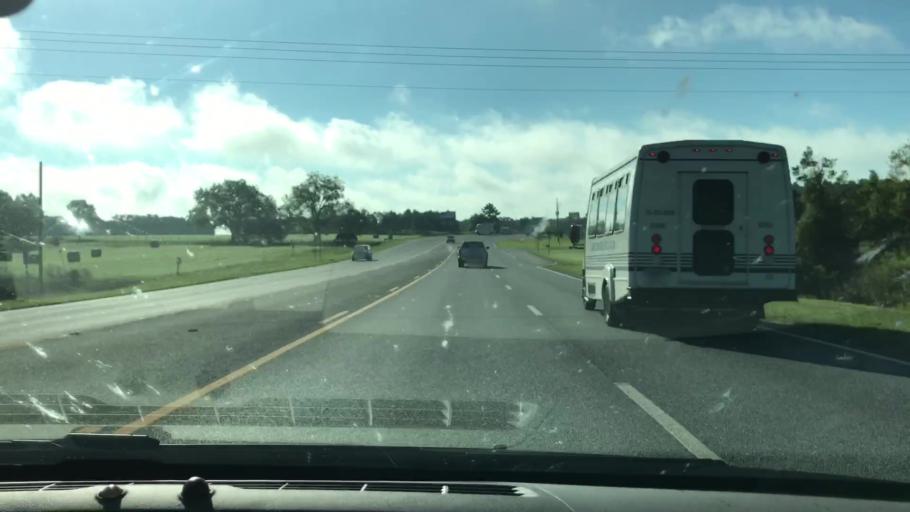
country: US
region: Georgia
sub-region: Terrell County
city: Dawson
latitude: 31.7580
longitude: -84.4297
